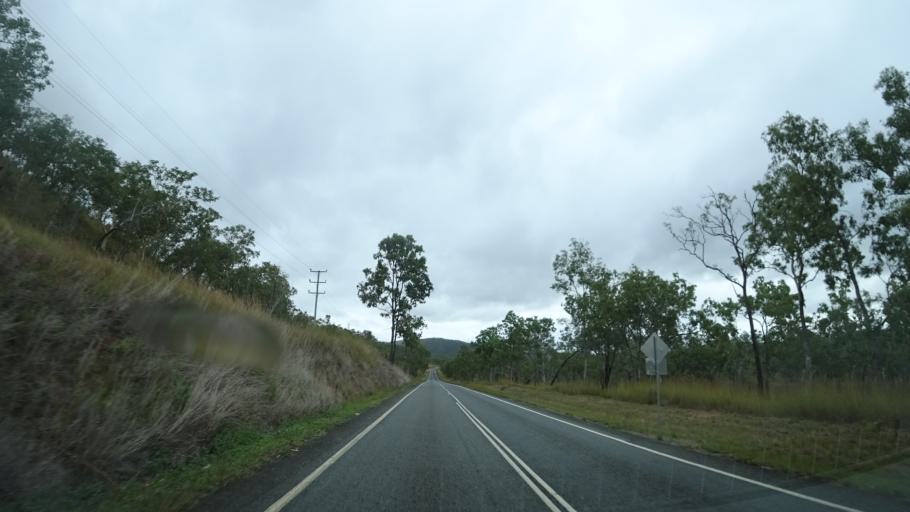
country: AU
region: Queensland
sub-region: Cairns
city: Port Douglas
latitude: -16.7096
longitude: 145.3499
